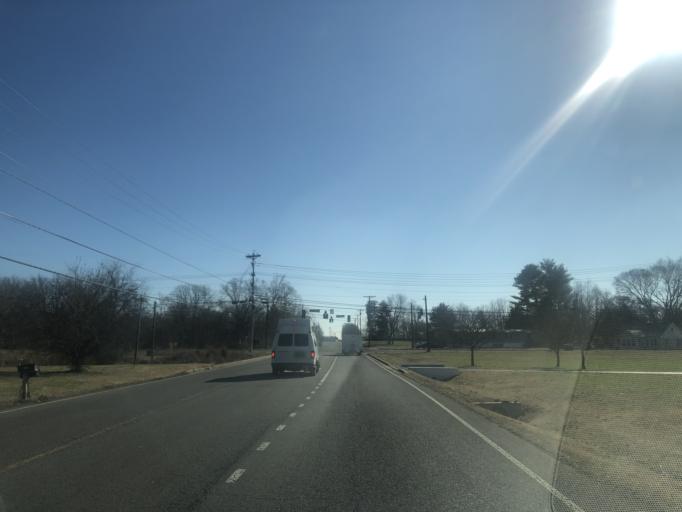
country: US
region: Tennessee
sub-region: Rutherford County
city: Smyrna
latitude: 35.9143
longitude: -86.4707
